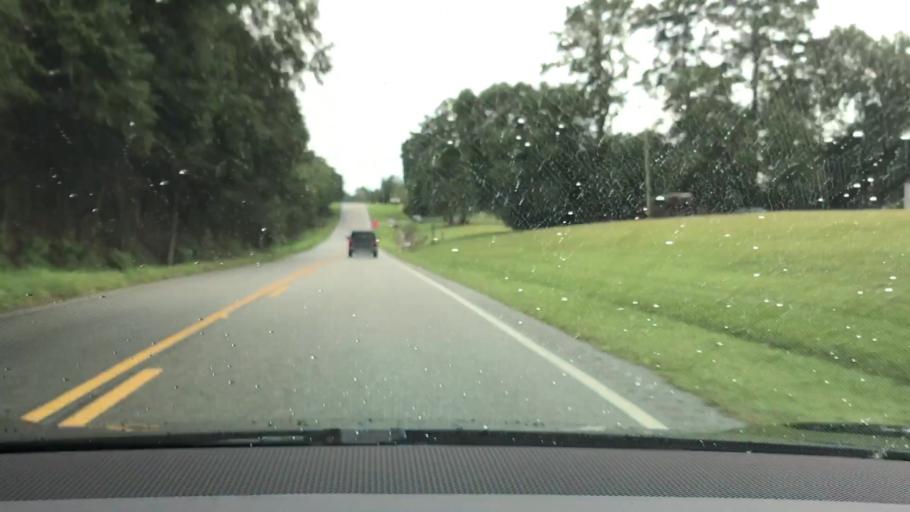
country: US
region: Alabama
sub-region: Geneva County
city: Samson
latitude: 31.0774
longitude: -86.1046
